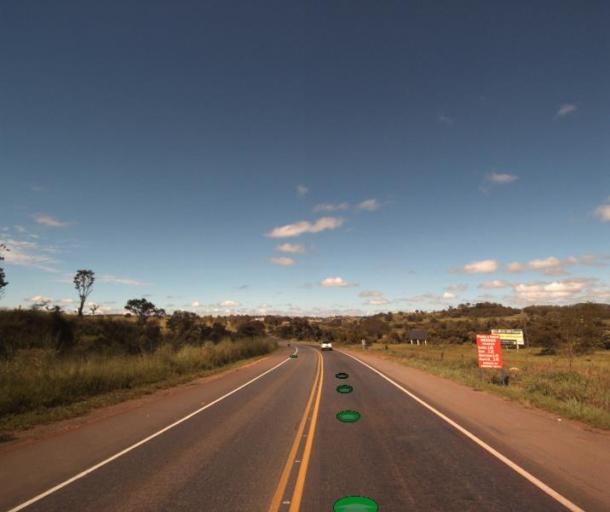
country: BR
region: Goias
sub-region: Rialma
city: Rialma
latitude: -15.2898
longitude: -49.5677
